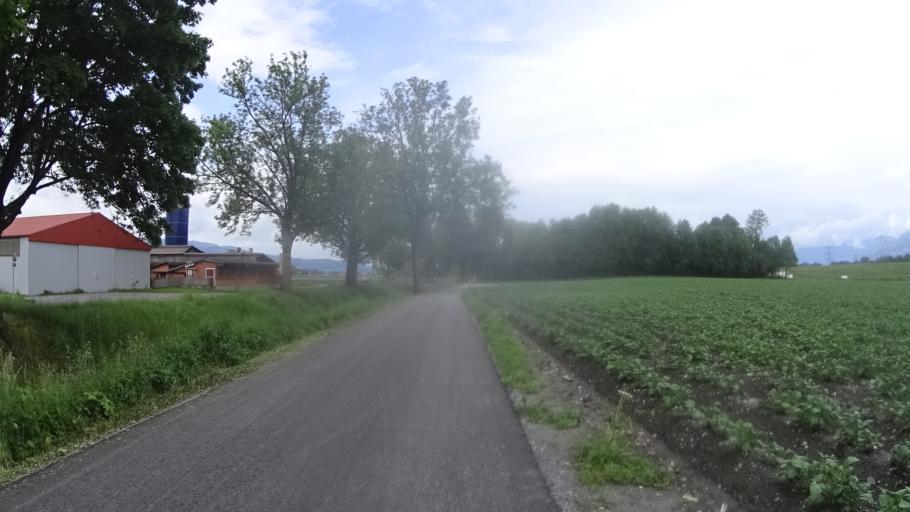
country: AT
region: Vorarlberg
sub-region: Politischer Bezirk Feldkirch
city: Koblach
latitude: 47.3471
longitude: 9.5961
